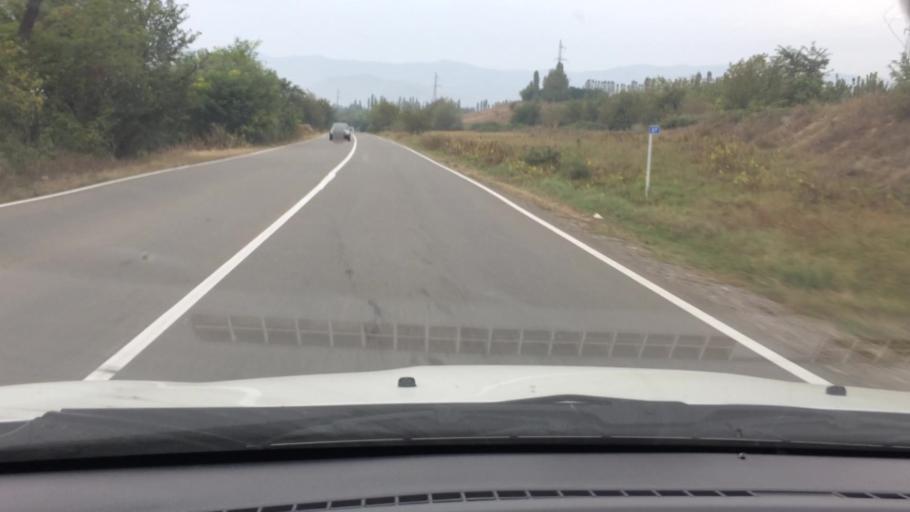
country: AM
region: Tavush
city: Bagratashen
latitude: 41.2738
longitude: 44.7904
